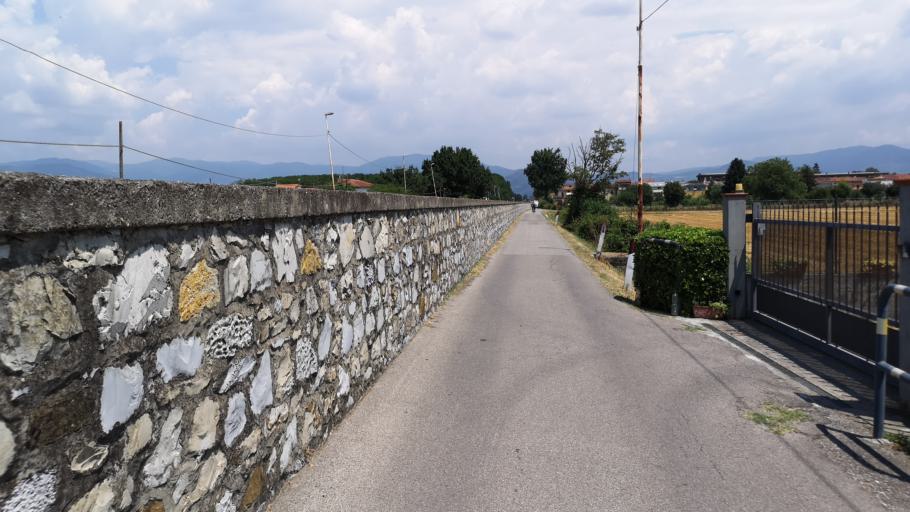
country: IT
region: Tuscany
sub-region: Provincia di Pistoia
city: Catena
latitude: 43.8615
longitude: 11.0354
